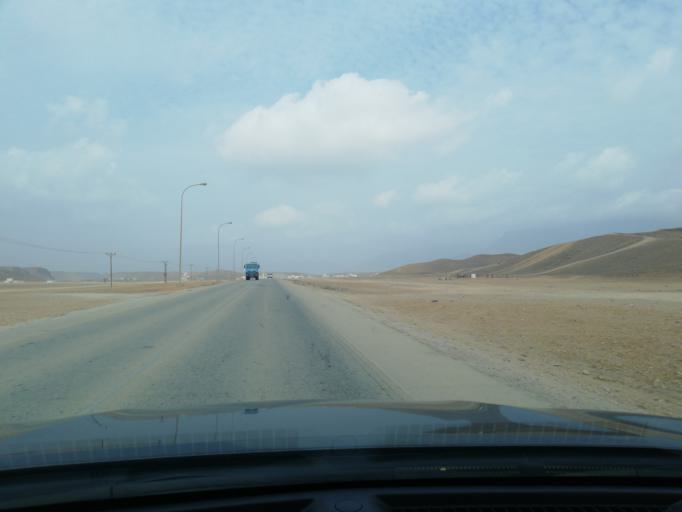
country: OM
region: Zufar
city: Salalah
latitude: 16.9609
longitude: 53.8784
